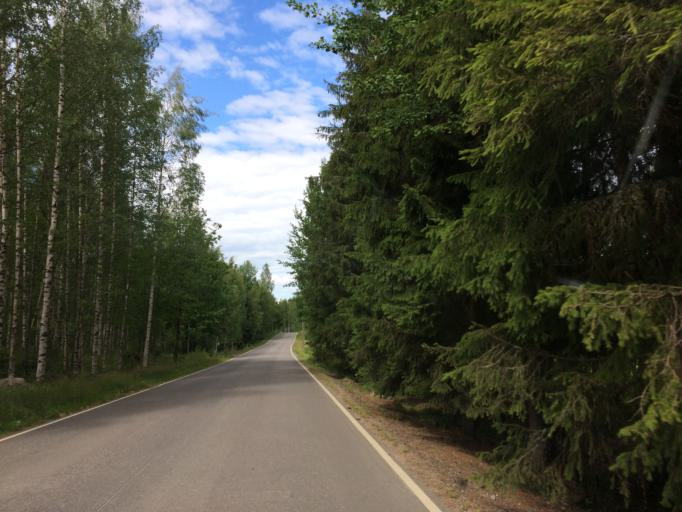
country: FI
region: Haeme
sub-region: Haemeenlinna
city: Janakkala
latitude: 60.8412
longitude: 24.5282
